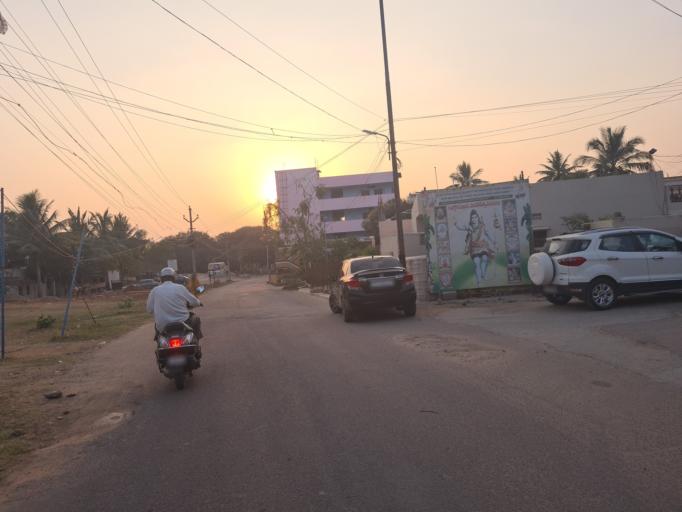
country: IN
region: Telangana
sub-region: Medak
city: Serilingampalle
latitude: 17.4788
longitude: 78.2988
